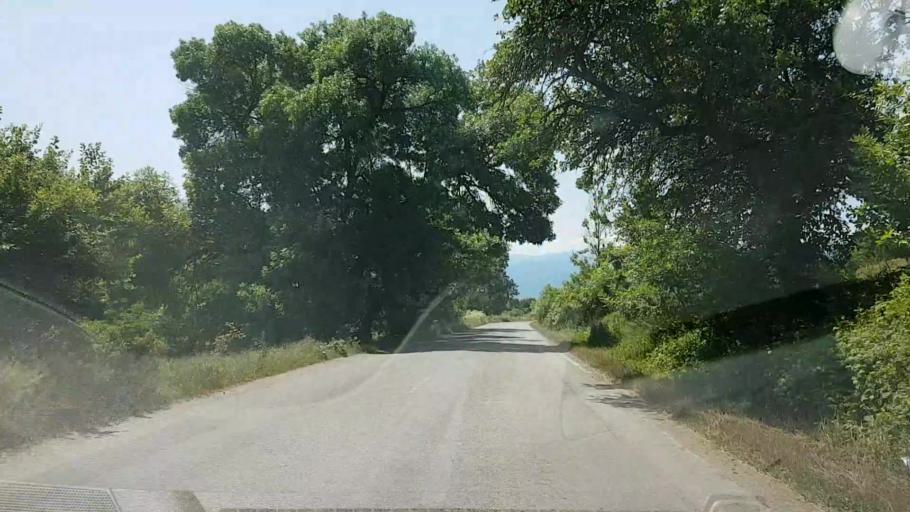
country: RO
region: Brasov
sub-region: Comuna Voila
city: Voila
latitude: 45.8468
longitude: 24.8330
